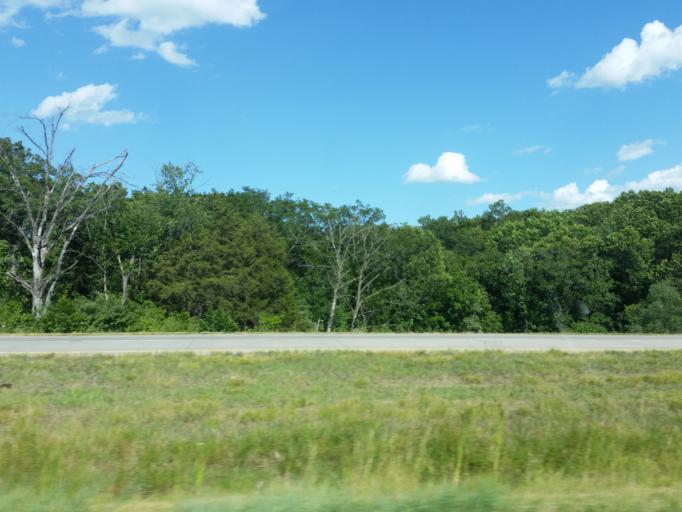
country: US
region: Missouri
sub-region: Lewis County
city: Canton
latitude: 40.1425
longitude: -91.5394
